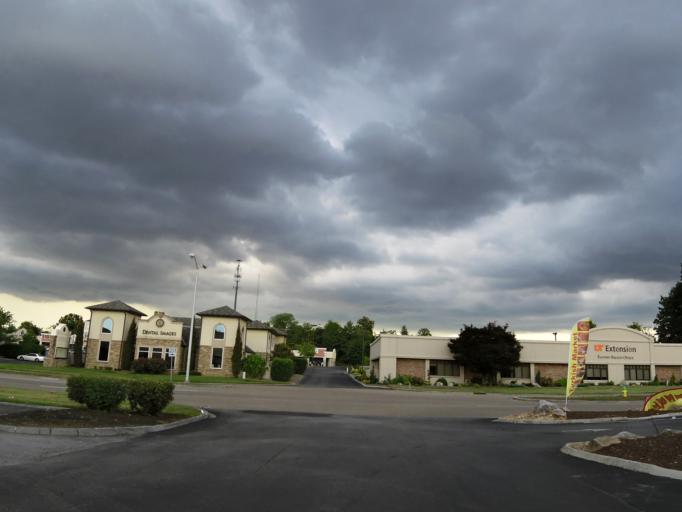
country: US
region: Tennessee
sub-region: Blount County
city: Louisville
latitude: 35.9233
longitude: -84.0505
